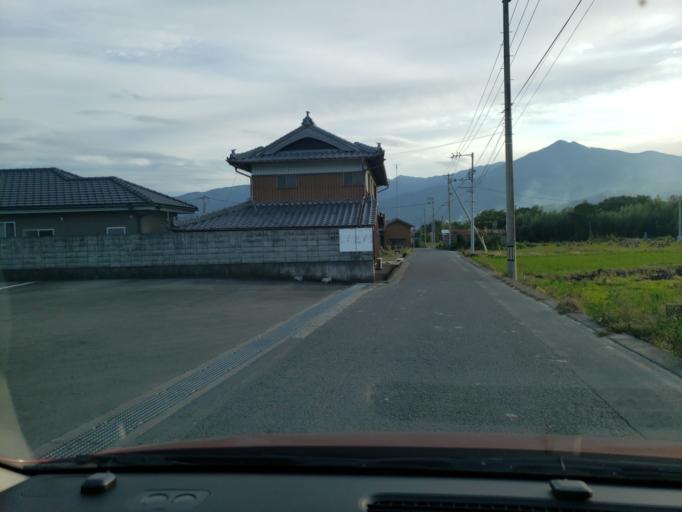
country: JP
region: Tokushima
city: Wakimachi
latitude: 34.0795
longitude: 134.2284
